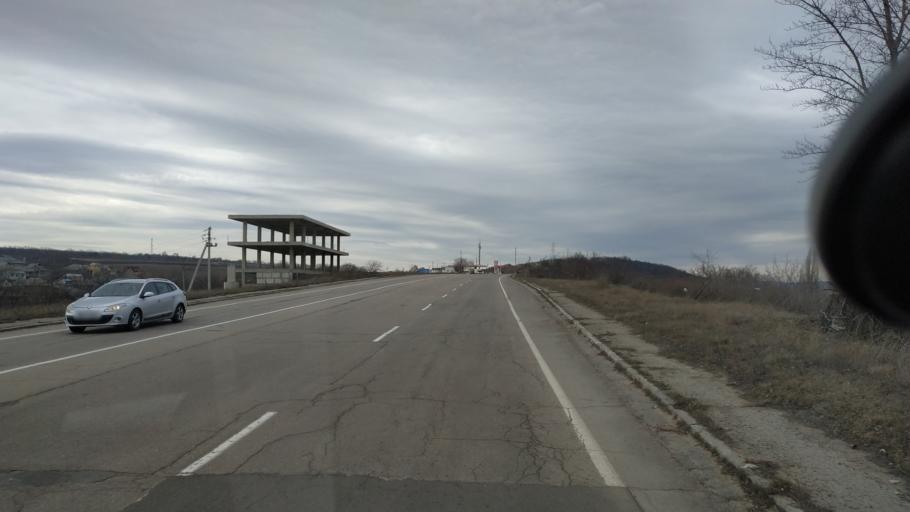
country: MD
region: Chisinau
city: Vadul lui Voda
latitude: 47.0860
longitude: 29.0752
